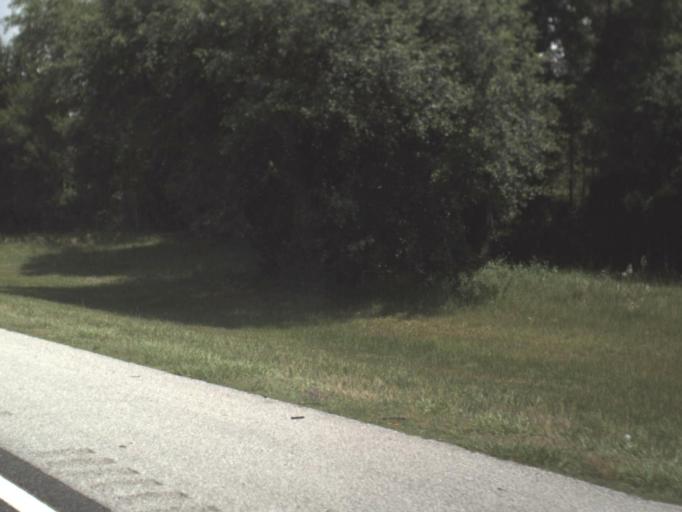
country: US
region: Florida
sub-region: Suwannee County
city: Wellborn
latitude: 30.3157
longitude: -82.8053
